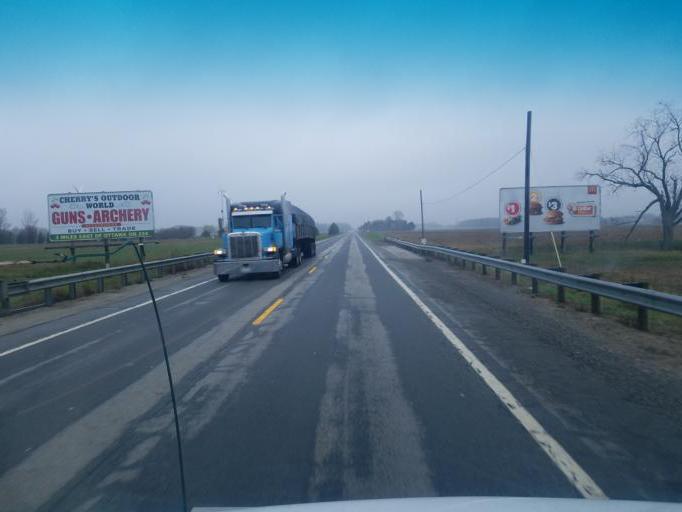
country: US
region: Ohio
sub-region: Wood County
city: Weston
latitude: 41.3722
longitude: -83.7521
